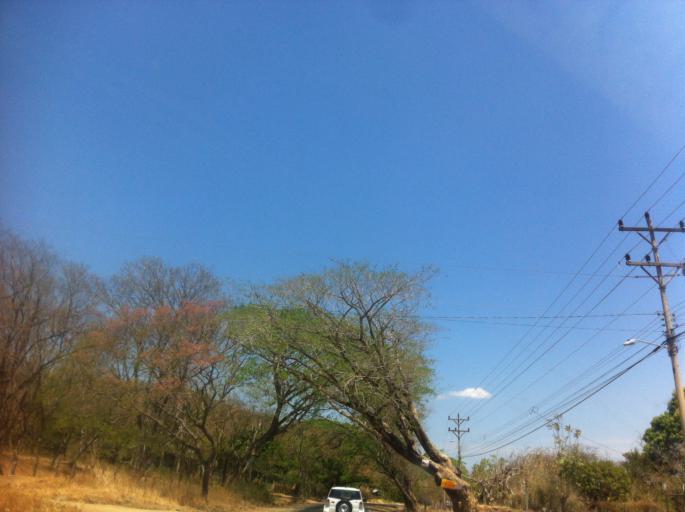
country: CR
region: Guanacaste
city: Belen
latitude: 10.3808
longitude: -85.5820
